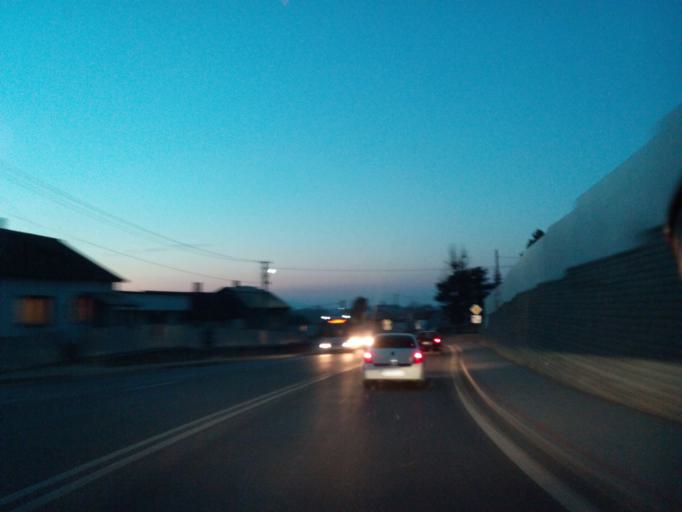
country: SK
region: Kosicky
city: Trebisov
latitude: 48.6984
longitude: 21.8070
